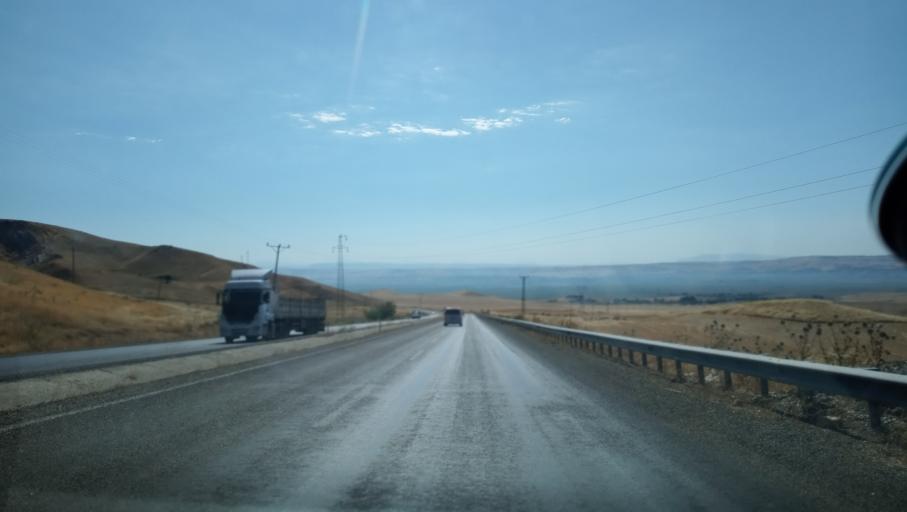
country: TR
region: Diyarbakir
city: Malabadi
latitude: 38.1187
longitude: 41.1329
